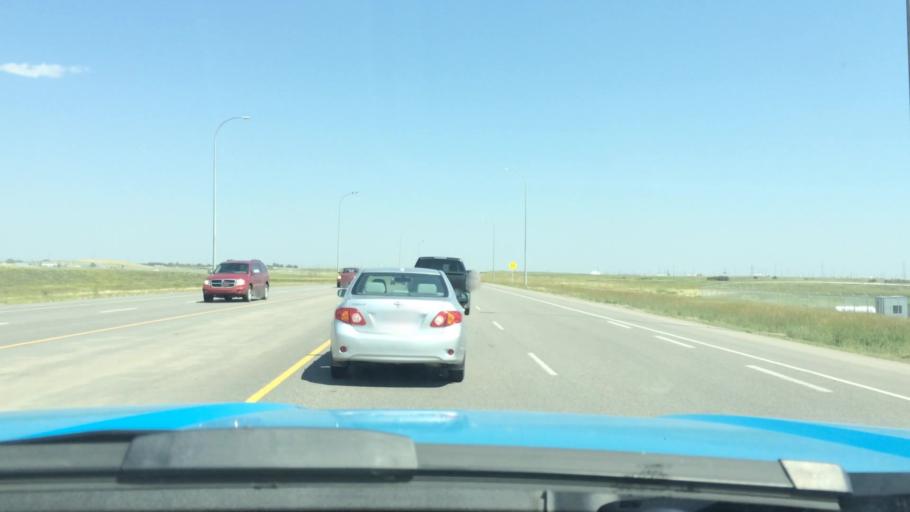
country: CA
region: Alberta
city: Chestermere
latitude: 51.0148
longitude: -113.9520
